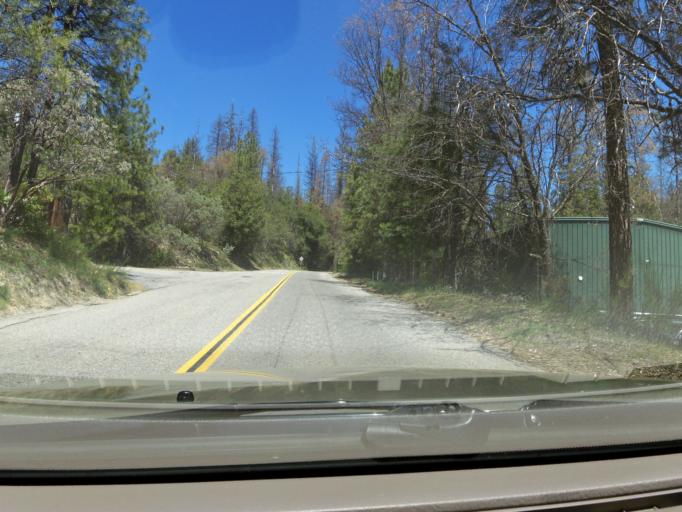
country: US
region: California
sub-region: Madera County
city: Oakhurst
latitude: 37.3209
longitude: -119.5566
